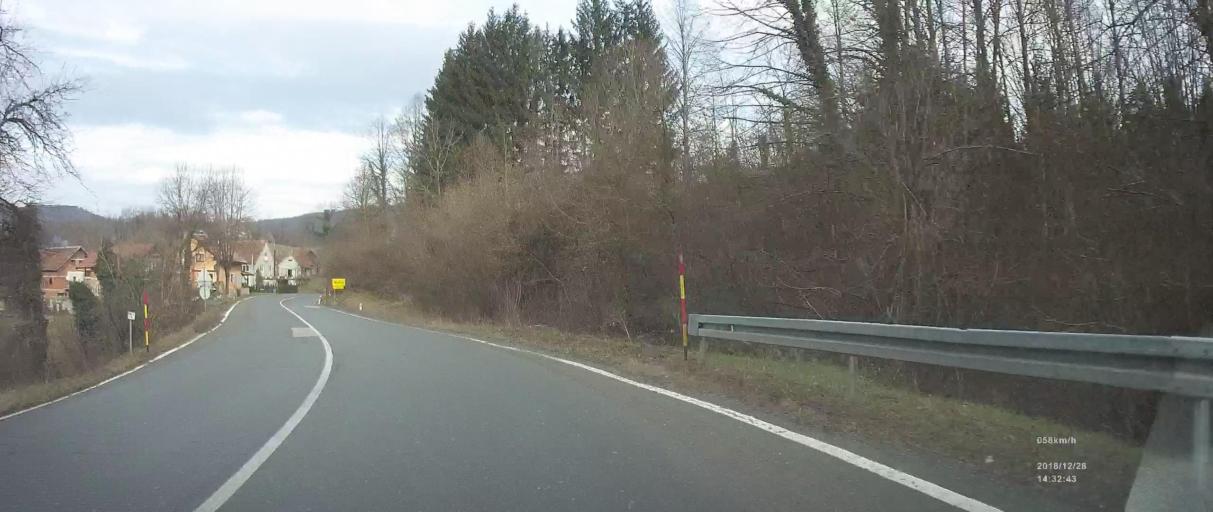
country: HR
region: Primorsko-Goranska
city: Vrbovsko
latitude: 45.4111
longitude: 15.1578
